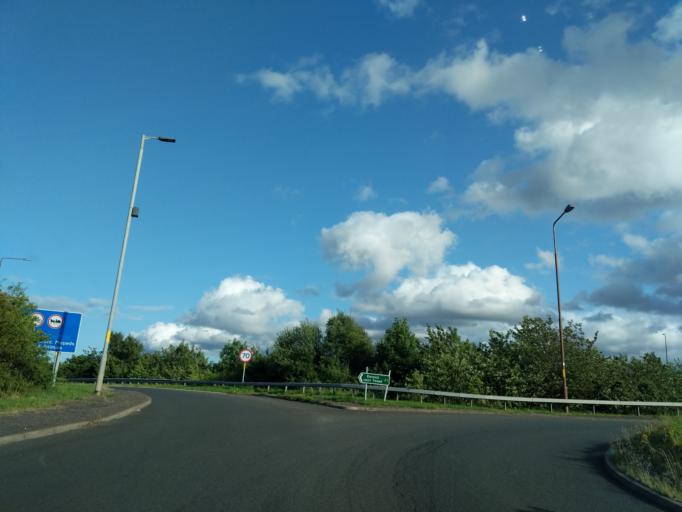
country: GB
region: Scotland
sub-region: East Lothian
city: Macmerry
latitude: 55.9509
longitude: -2.8803
